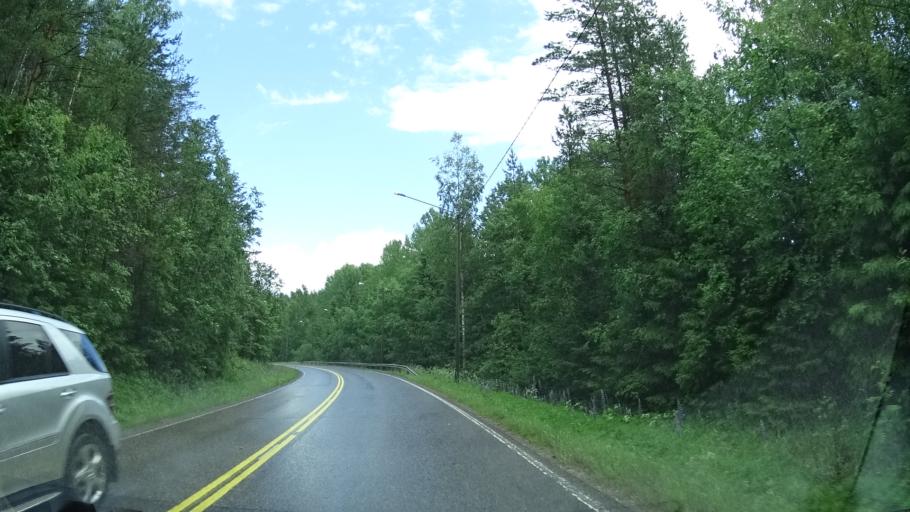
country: FI
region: Uusimaa
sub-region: Helsinki
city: Espoo
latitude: 60.3350
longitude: 24.6528
